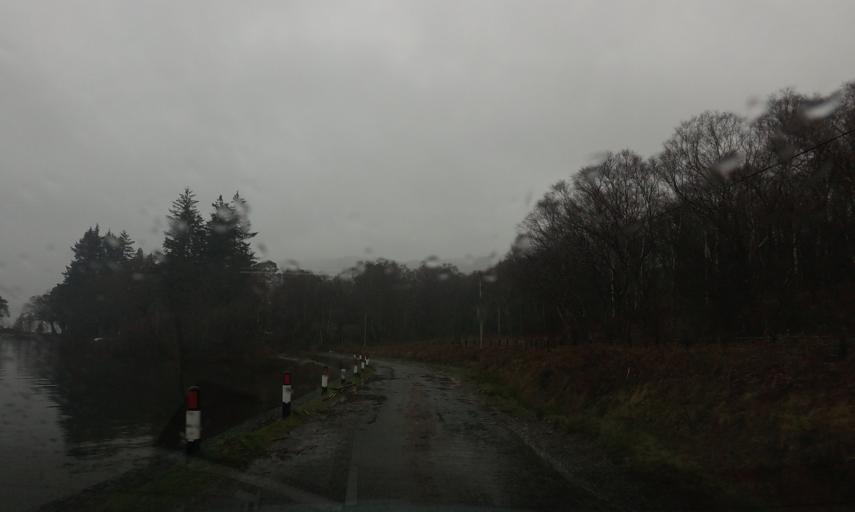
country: GB
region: Scotland
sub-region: West Dunbartonshire
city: Balloch
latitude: 56.1506
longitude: -4.6419
